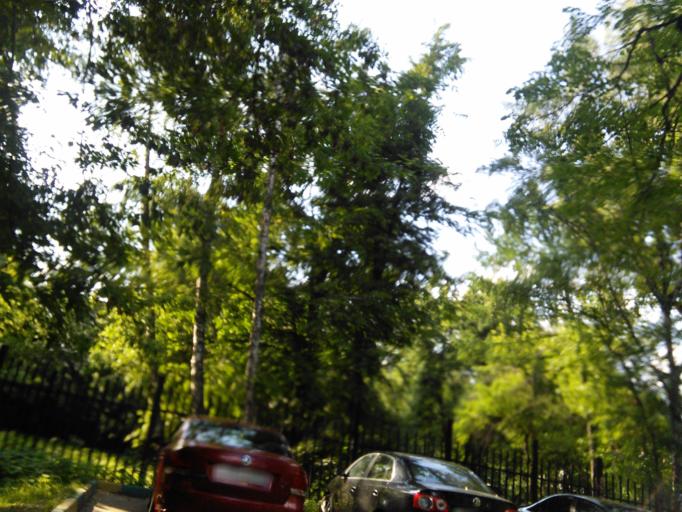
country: RU
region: Moskovskaya
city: Bogorodskoye
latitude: 55.8141
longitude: 37.7160
